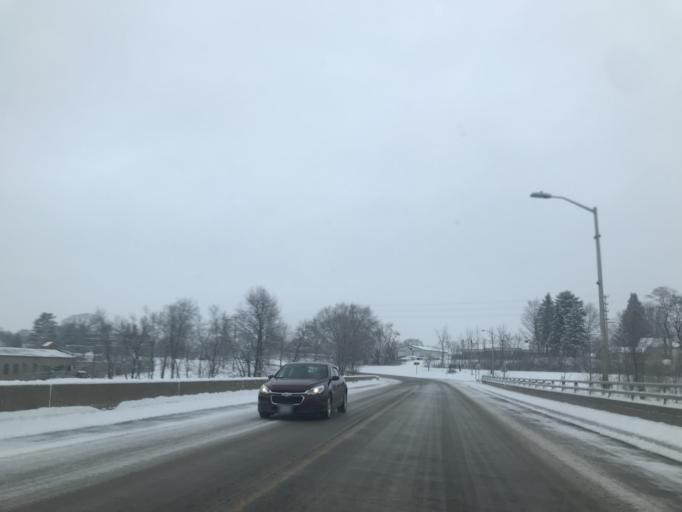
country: US
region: Wisconsin
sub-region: Oconto County
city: Oconto Falls
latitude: 44.8748
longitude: -88.1471
